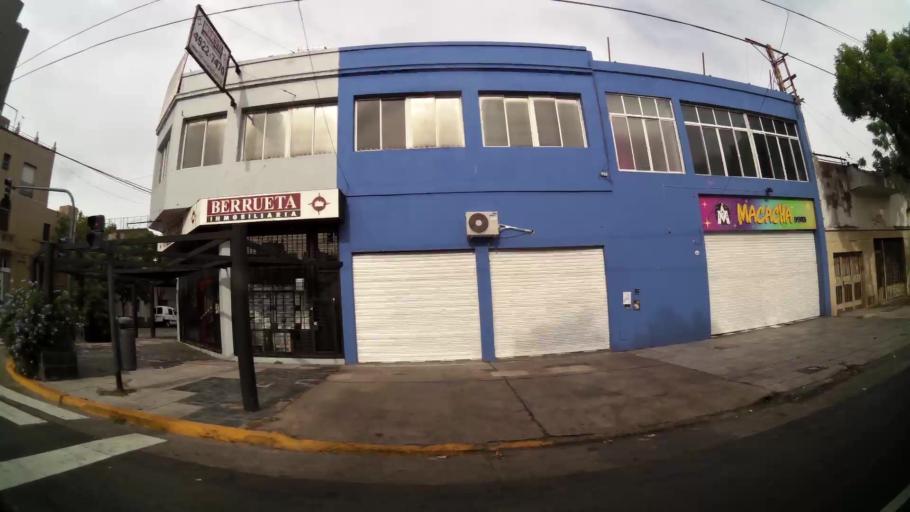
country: AR
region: Buenos Aires F.D.
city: Villa Santa Rita
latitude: -34.6350
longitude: -58.4325
